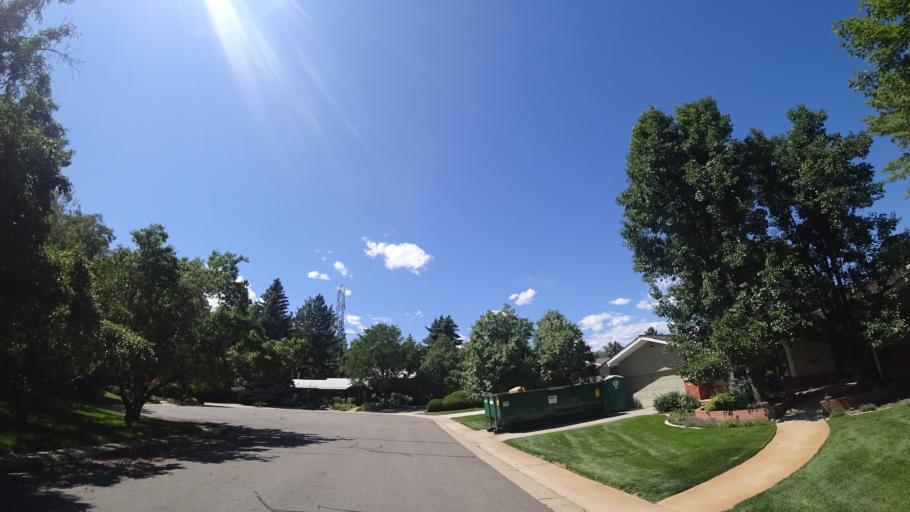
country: US
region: Colorado
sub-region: Arapahoe County
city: Greenwood Village
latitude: 39.6075
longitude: -104.9750
